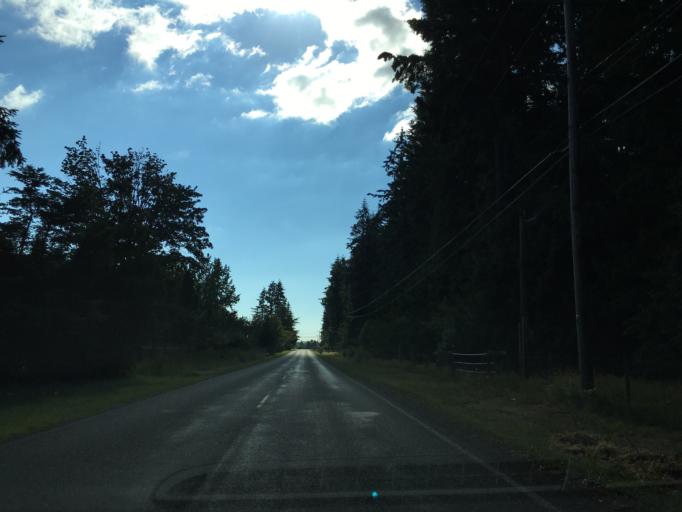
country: US
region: Washington
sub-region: Whatcom County
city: Ferndale
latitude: 48.9207
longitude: -122.5618
